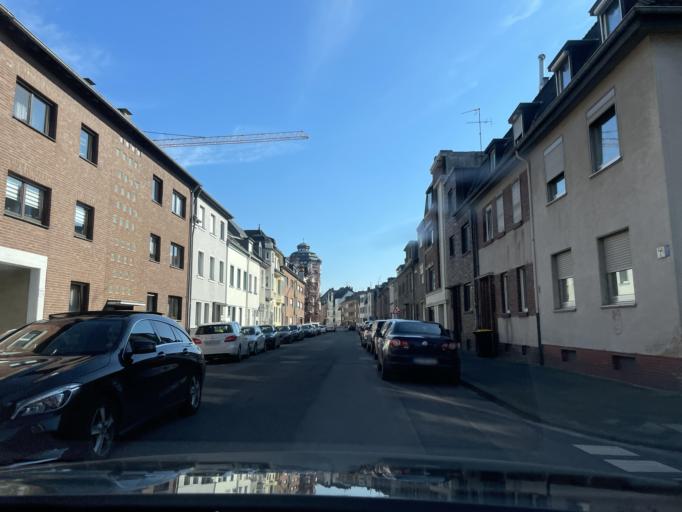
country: DE
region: North Rhine-Westphalia
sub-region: Regierungsbezirk Dusseldorf
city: Monchengladbach
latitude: 51.2032
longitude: 6.4236
